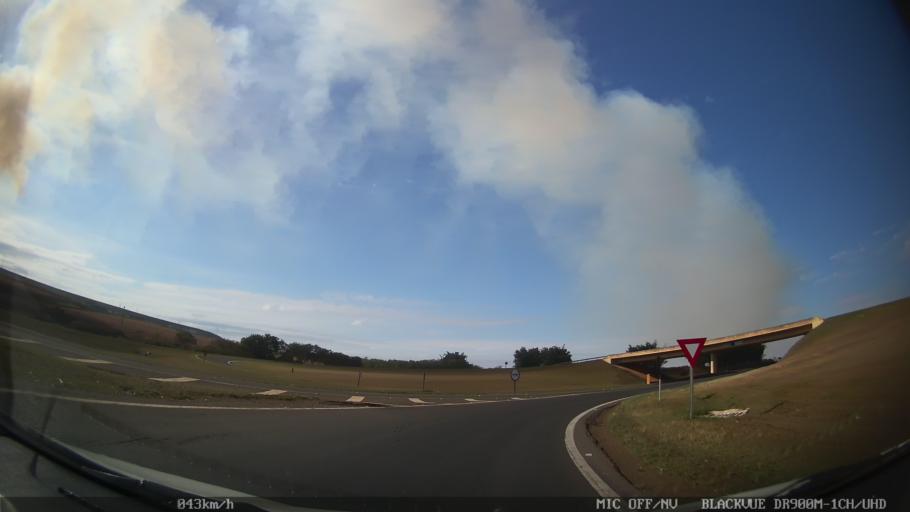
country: BR
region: Sao Paulo
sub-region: Piracicaba
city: Piracicaba
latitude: -22.6998
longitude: -47.6029
